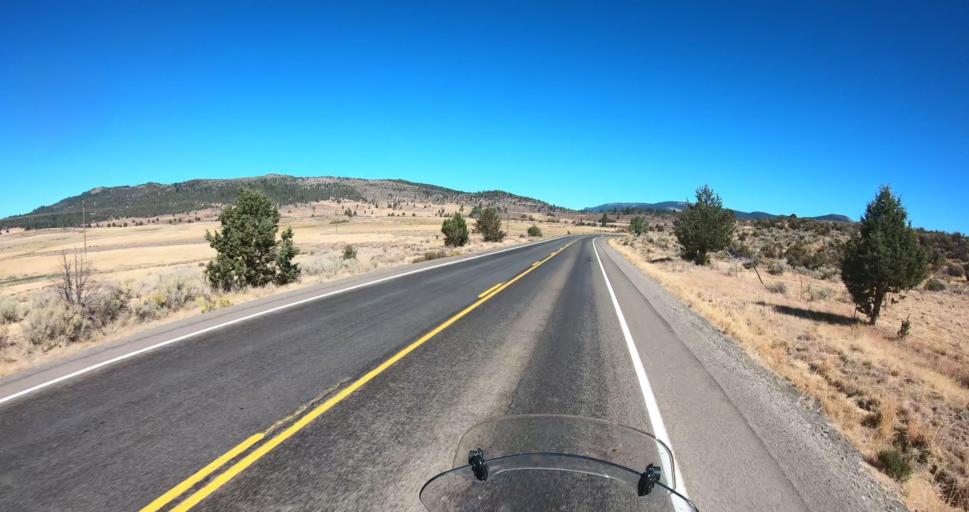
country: US
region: Oregon
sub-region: Lake County
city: Lakeview
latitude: 42.3214
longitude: -120.3312
